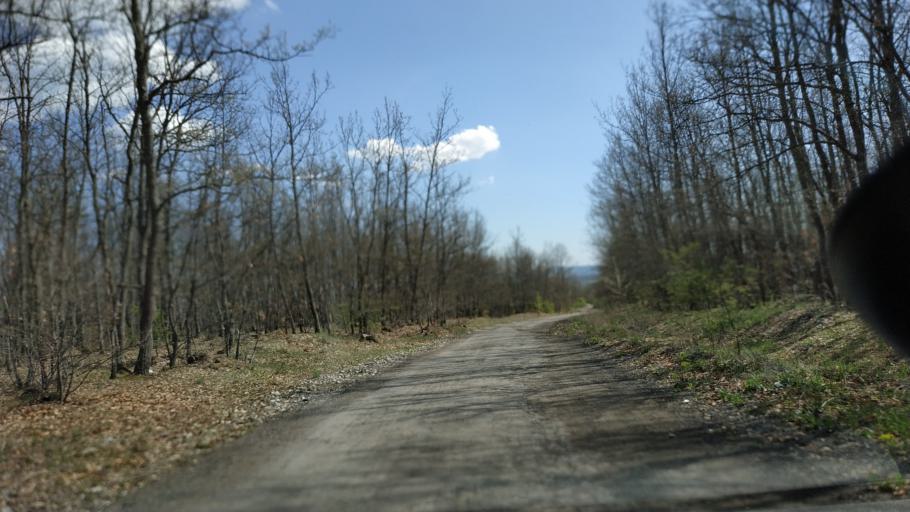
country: RS
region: Central Serbia
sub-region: Zajecarski Okrug
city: Soko Banja
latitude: 43.5364
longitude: 21.9061
